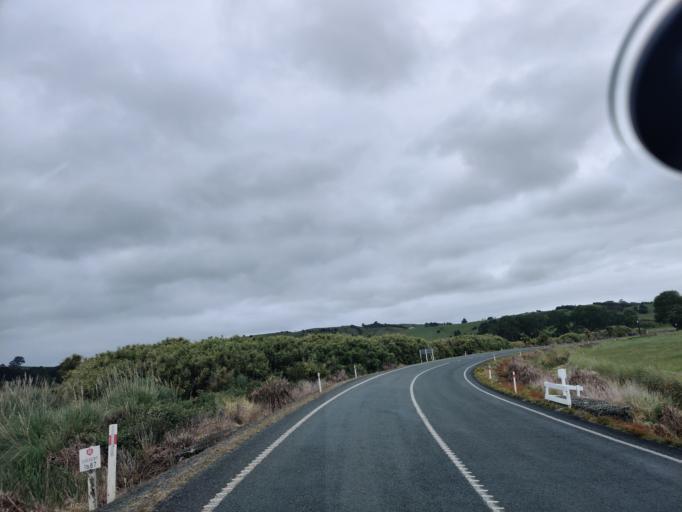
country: NZ
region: Northland
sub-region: Kaipara District
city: Dargaville
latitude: -36.1195
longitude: 174.1004
